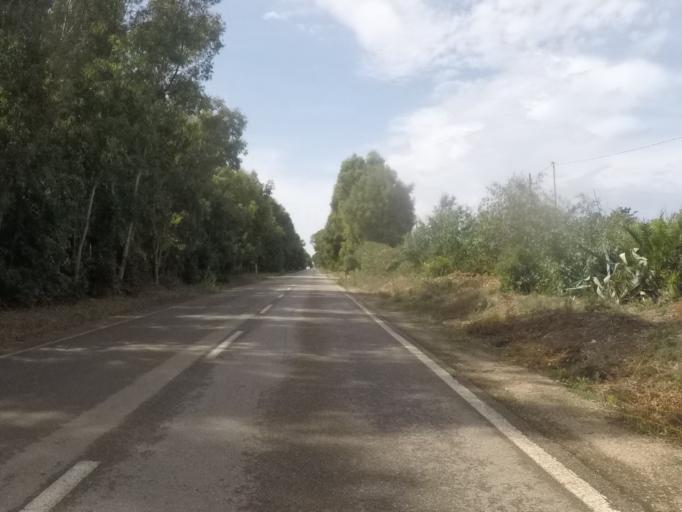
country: IT
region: Sardinia
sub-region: Provincia di Sassari
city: Alghero
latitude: 40.6561
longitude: 8.2343
